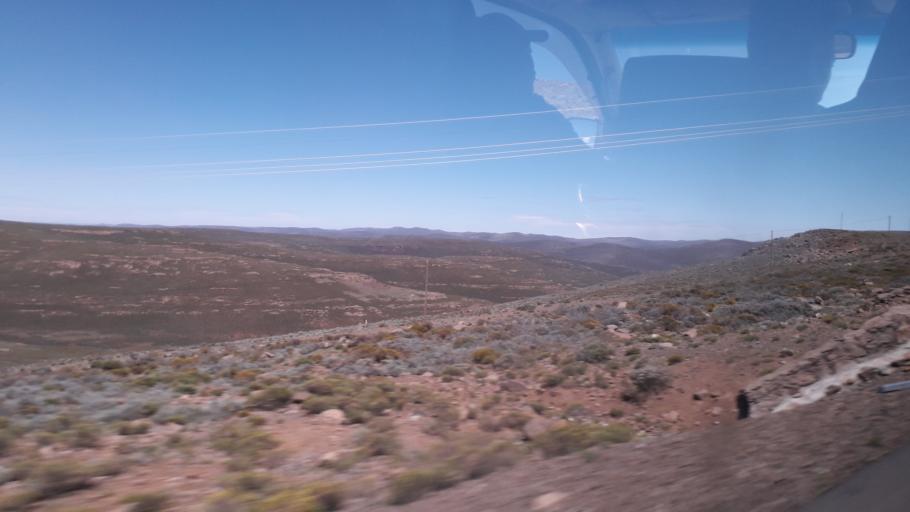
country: LS
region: Mokhotlong
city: Mokhotlong
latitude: -29.0255
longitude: 28.8597
